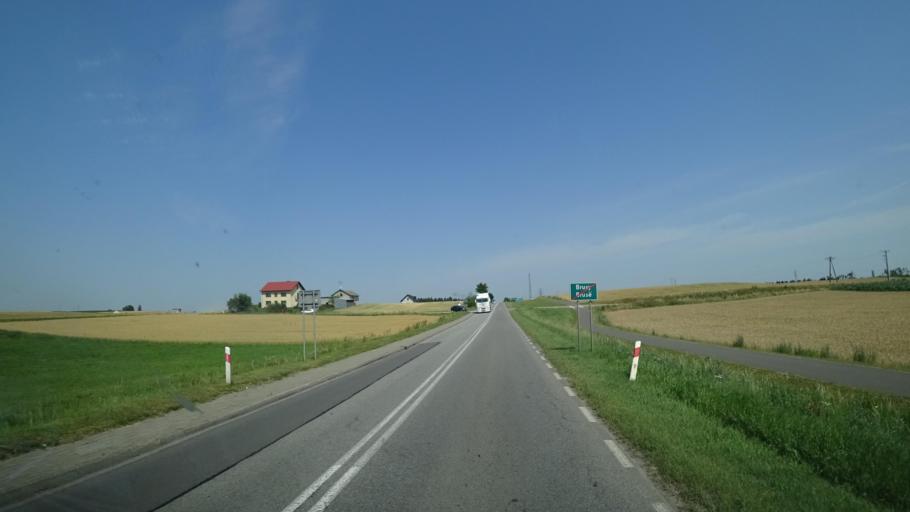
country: PL
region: Pomeranian Voivodeship
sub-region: Powiat chojnicki
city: Brusy
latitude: 53.8949
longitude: 17.7235
